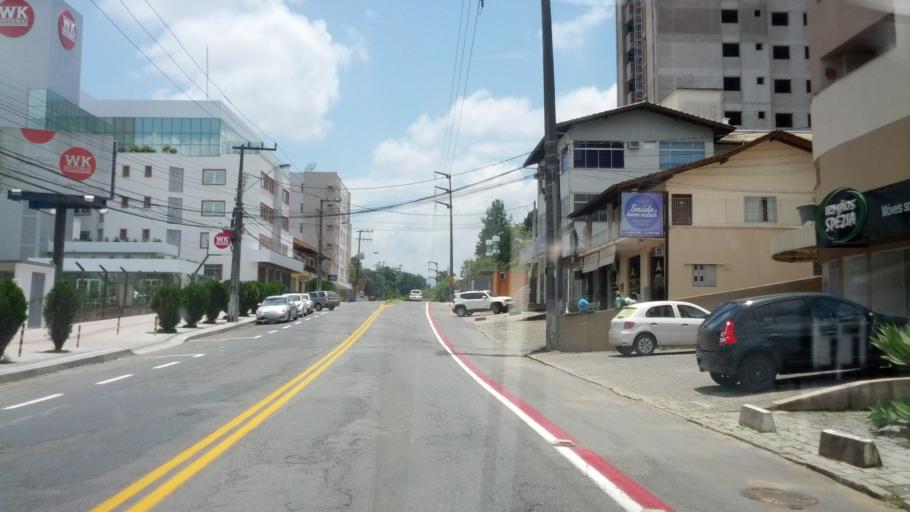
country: BR
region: Santa Catarina
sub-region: Blumenau
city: Blumenau
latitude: -26.9004
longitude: -49.0883
